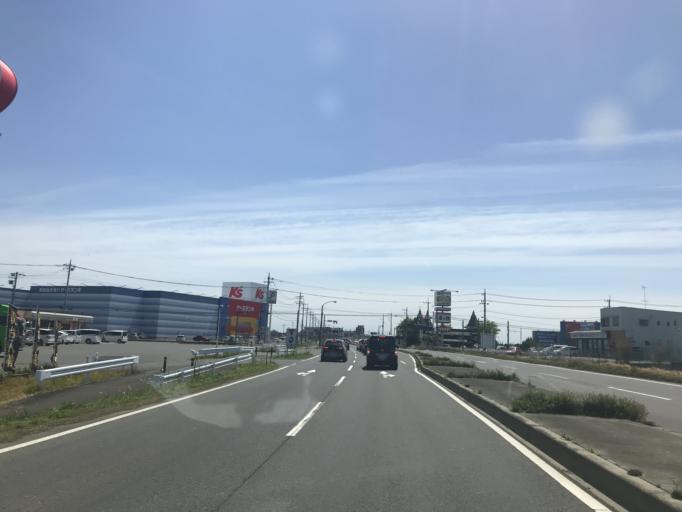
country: JP
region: Ibaraki
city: Ishige
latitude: 36.1998
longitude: 139.9846
